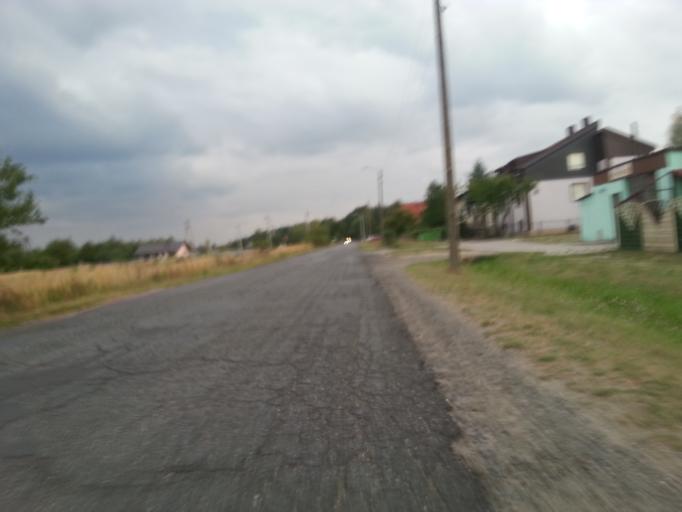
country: PL
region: Lower Silesian Voivodeship
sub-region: Powiat olesnicki
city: Twardogora
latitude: 51.3535
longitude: 17.4533
